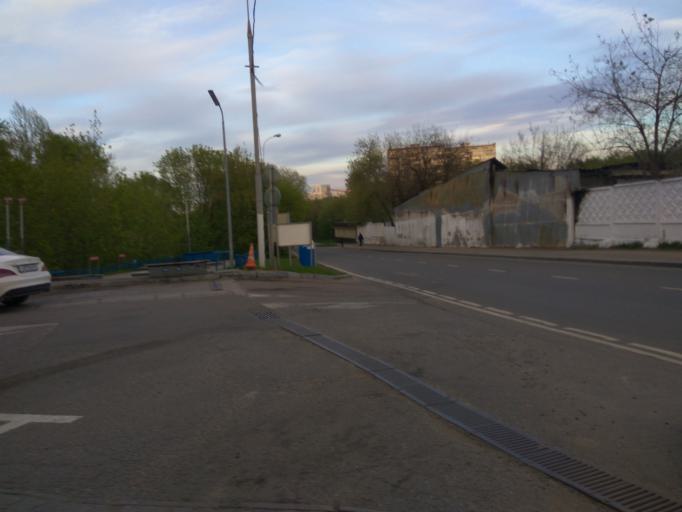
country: RU
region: Moscow
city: Kotlovka
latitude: 55.6842
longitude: 37.6064
